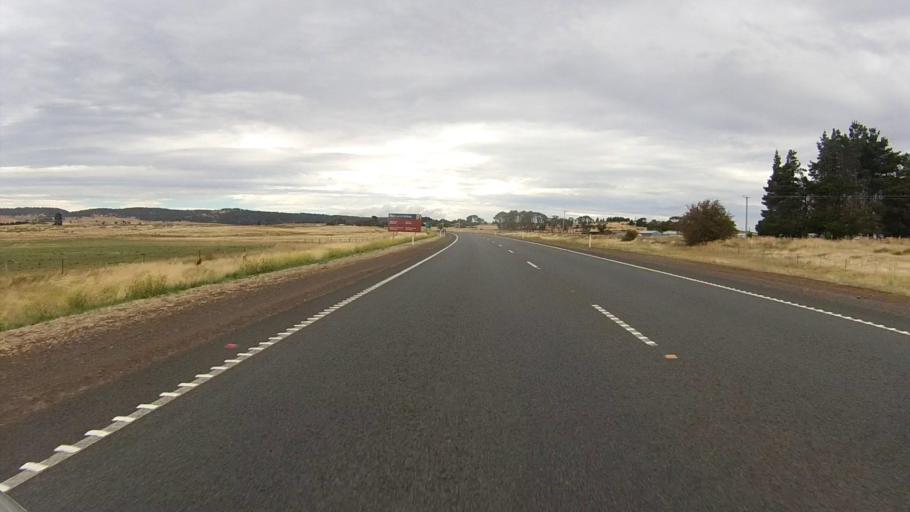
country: AU
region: Tasmania
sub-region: Brighton
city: Bridgewater
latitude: -42.3192
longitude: 147.3505
